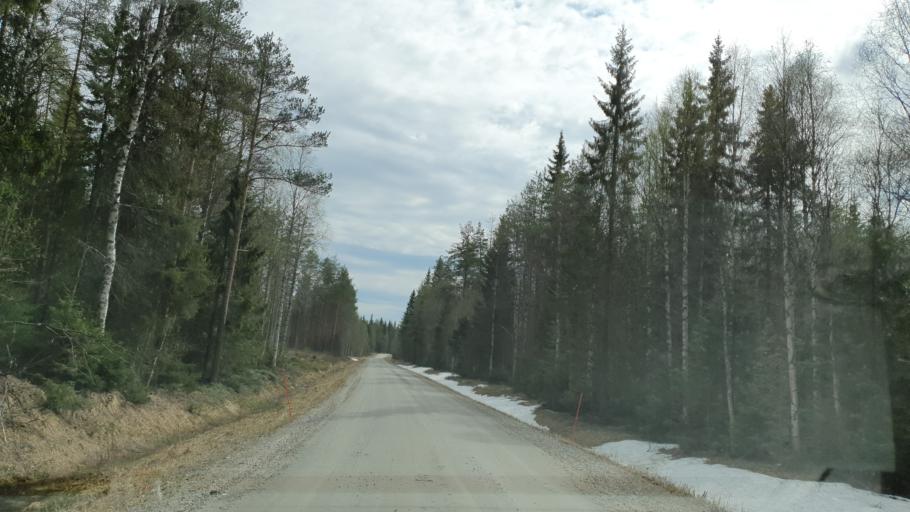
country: FI
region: Kainuu
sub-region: Kehys-Kainuu
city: Kuhmo
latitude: 64.1202
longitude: 29.9540
